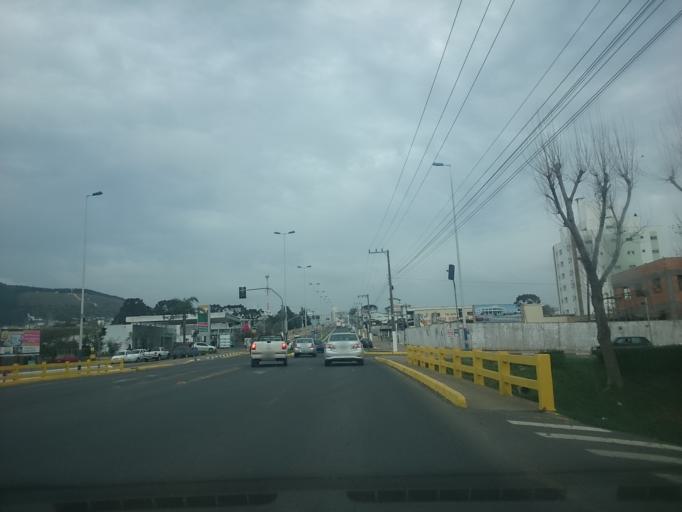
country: BR
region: Santa Catarina
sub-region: Lages
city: Lages
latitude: -27.8235
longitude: -50.3219
